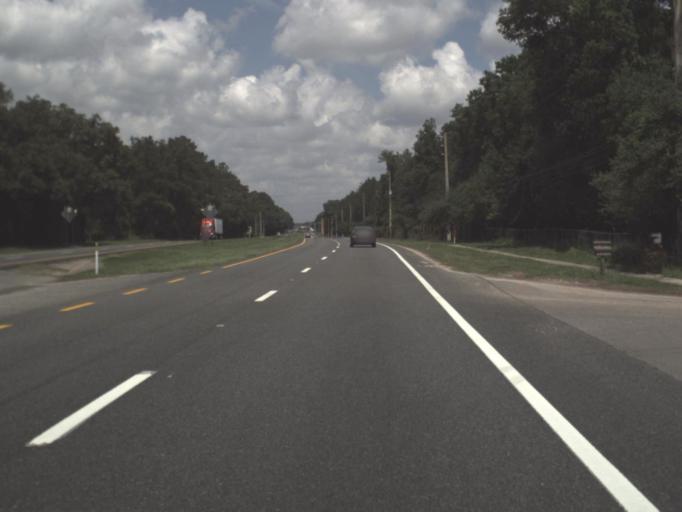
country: US
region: Florida
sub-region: Saint Johns County
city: Fruit Cove
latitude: 30.1459
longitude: -81.5203
